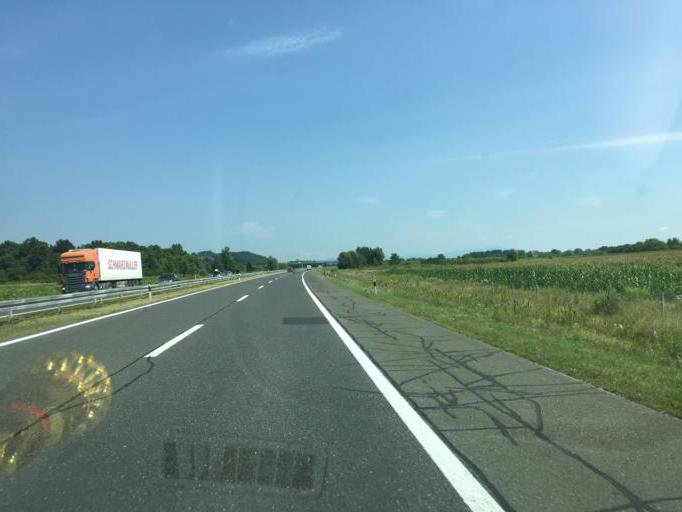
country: HR
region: Zagrebacka
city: Jakovlje
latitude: 45.9489
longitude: 15.8334
